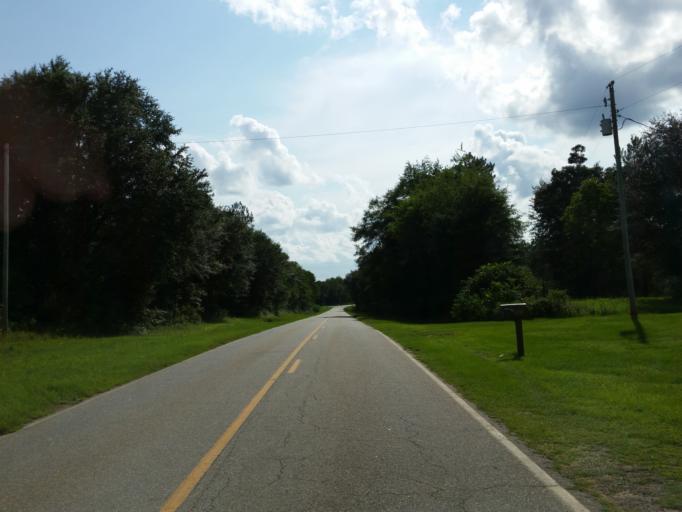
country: US
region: Georgia
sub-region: Lee County
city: Leesburg
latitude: 31.7741
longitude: -84.1092
